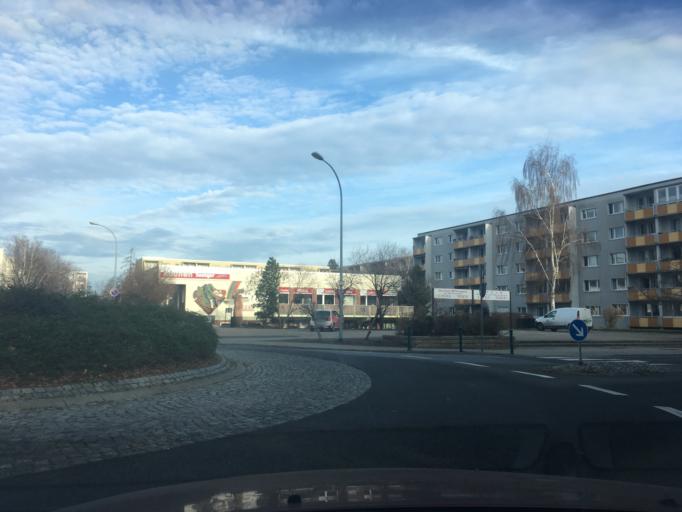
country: DE
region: Saxony
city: Bautzen
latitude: 51.1750
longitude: 14.4542
